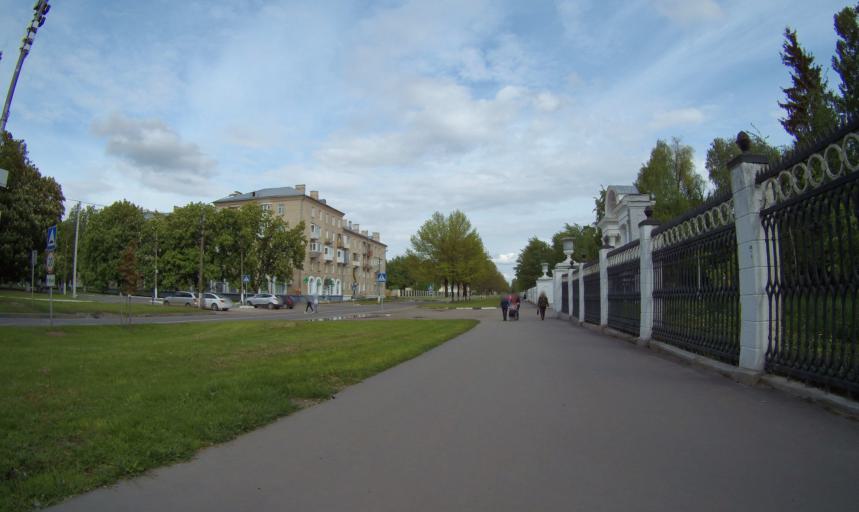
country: RU
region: Moskovskaya
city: Kolomna
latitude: 55.0882
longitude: 38.7782
